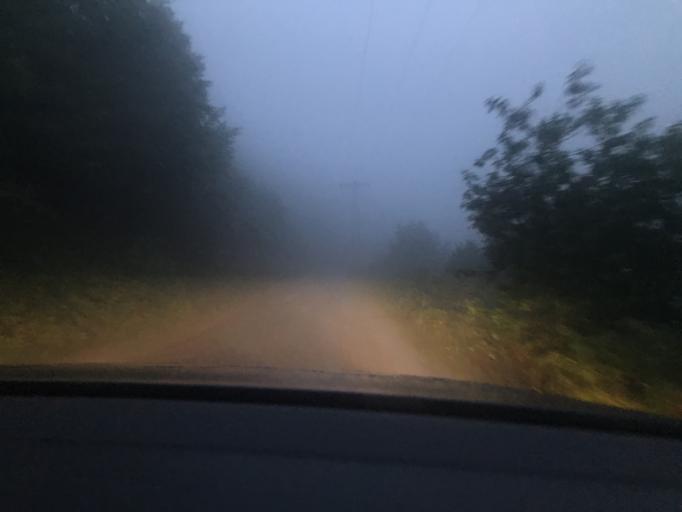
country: TR
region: Trabzon
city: Hayrat
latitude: 40.8358
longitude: 40.3868
